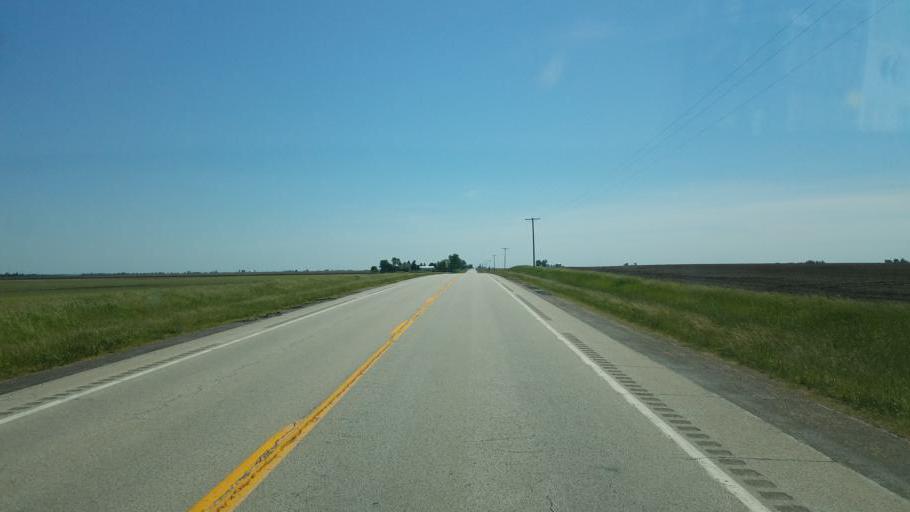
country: US
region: Illinois
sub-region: McLean County
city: Heyworth
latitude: 40.3123
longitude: -88.9119
